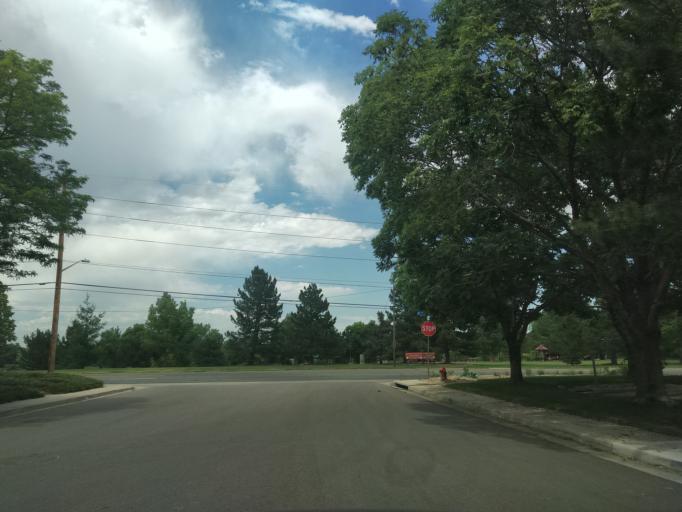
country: US
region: Colorado
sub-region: Jefferson County
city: Lakewood
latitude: 39.6817
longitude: -105.1056
